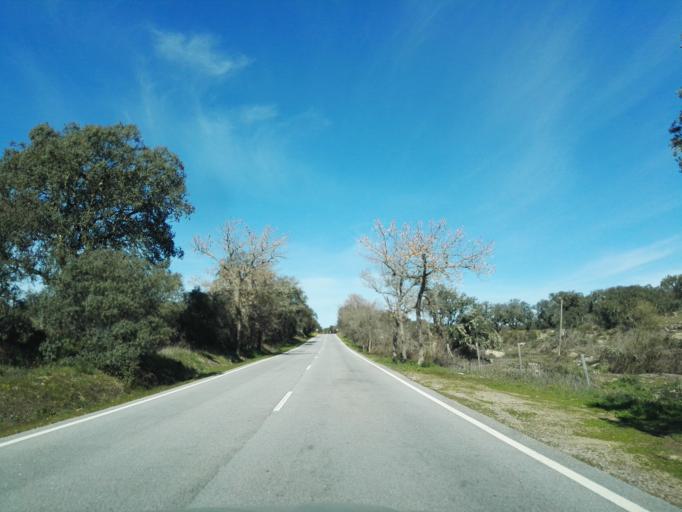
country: PT
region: Portalegre
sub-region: Arronches
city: Arronches
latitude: 39.0710
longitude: -7.2770
